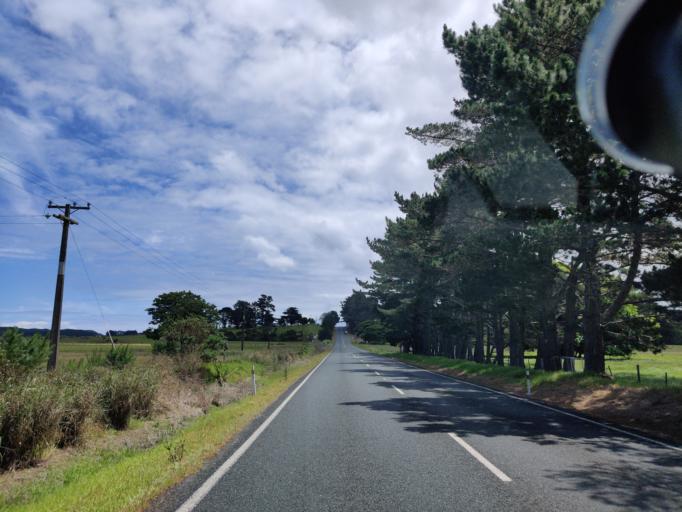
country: NZ
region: Northland
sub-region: Far North District
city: Kaitaia
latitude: -34.6802
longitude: 173.0064
